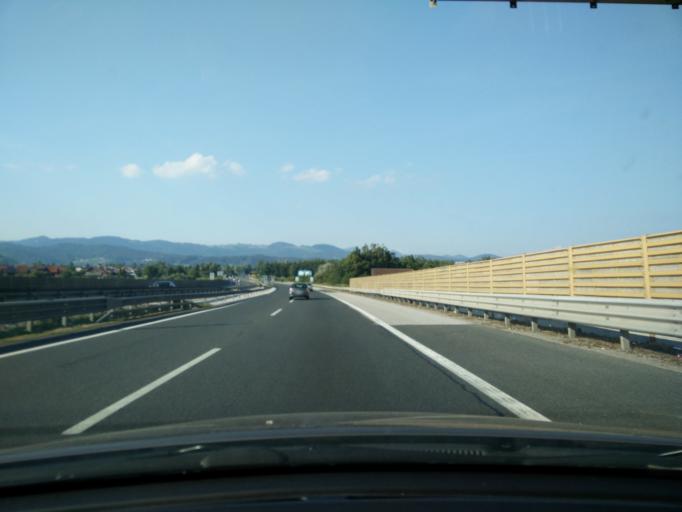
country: SI
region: Vrhnika
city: Verd
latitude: 45.9585
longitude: 14.3059
